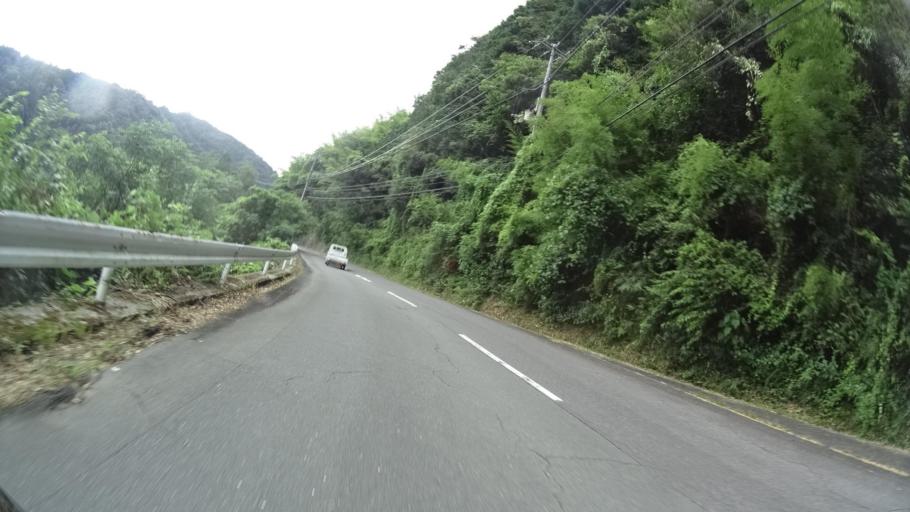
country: JP
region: Mie
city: Nabari
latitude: 34.7074
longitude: 136.0421
